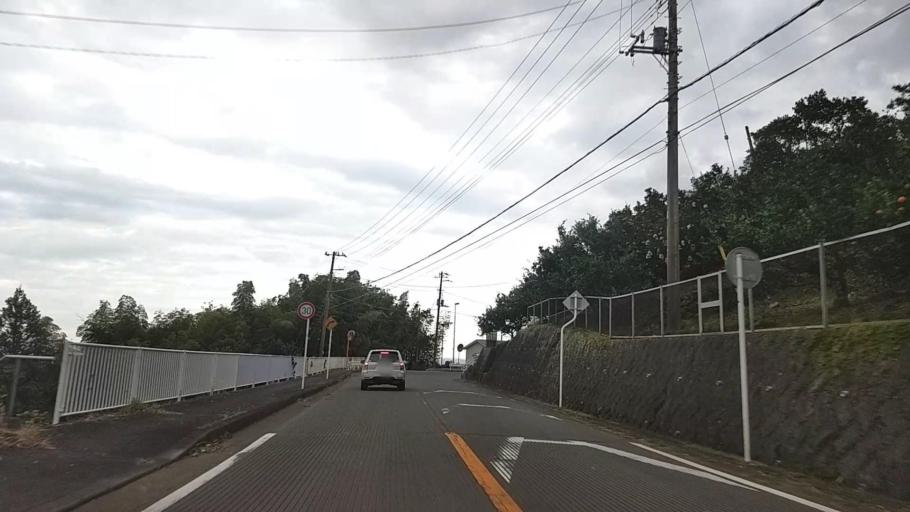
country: JP
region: Kanagawa
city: Yugawara
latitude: 35.1844
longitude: 139.1318
